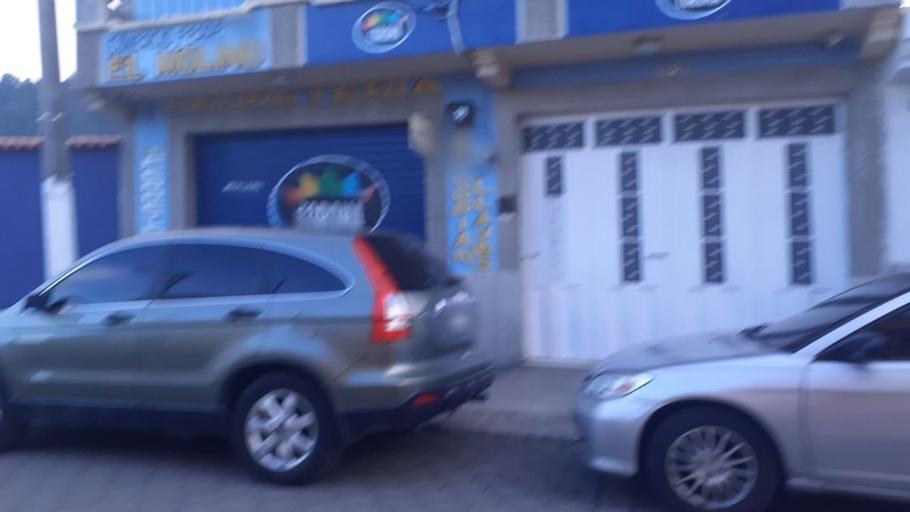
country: GT
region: Quetzaltenango
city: Quetzaltenango
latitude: 14.8325
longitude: -91.5253
